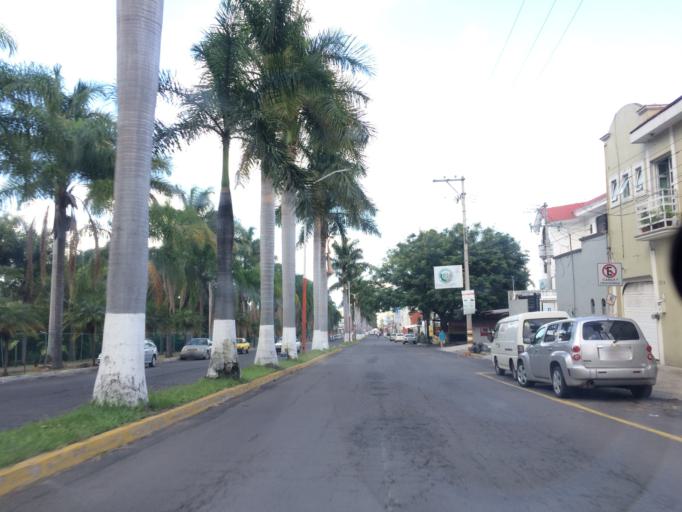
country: MX
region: Nayarit
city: Tepic
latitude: 21.5017
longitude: -104.9107
